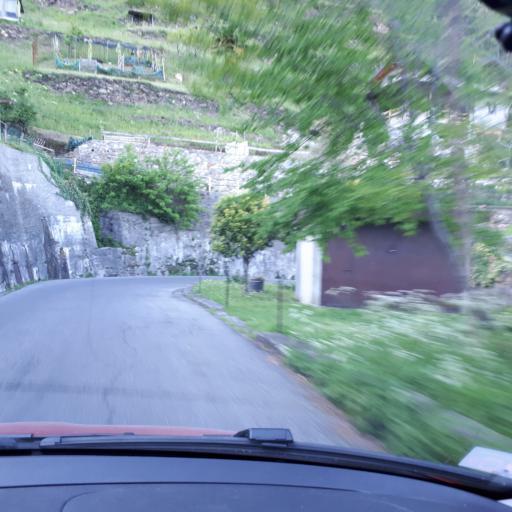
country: IT
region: Lombardy
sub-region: Provincia di Como
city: Musso
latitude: 46.1143
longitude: 9.2717
